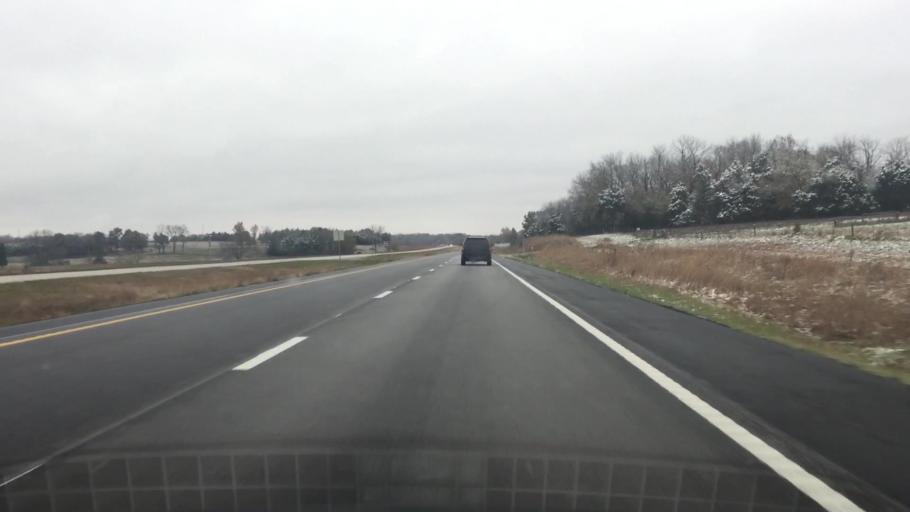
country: US
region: Missouri
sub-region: Saint Clair County
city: Osceola
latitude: 38.0001
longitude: -93.6547
